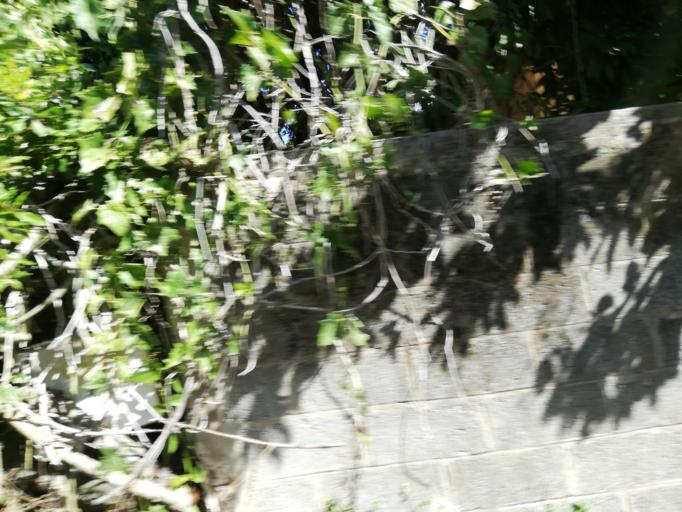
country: MU
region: Moka
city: Moka
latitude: -20.2265
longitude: 57.4763
